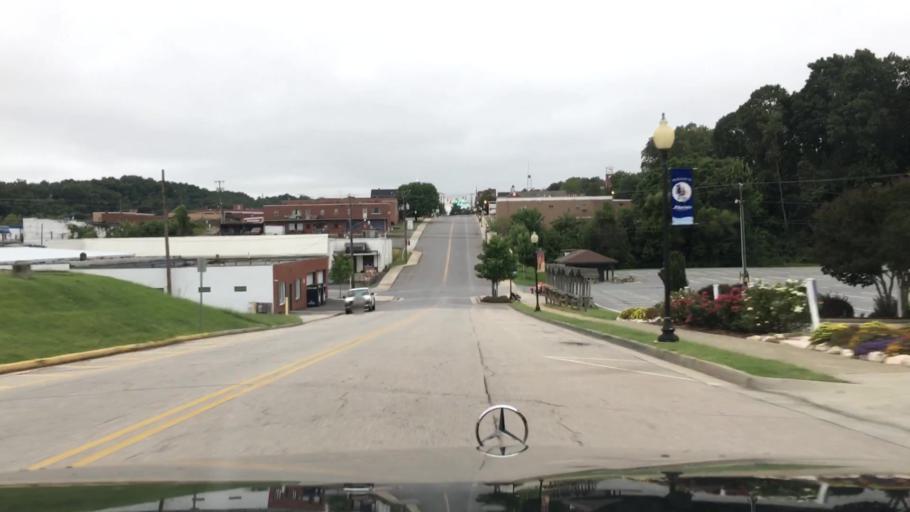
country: US
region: Virginia
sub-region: Campbell County
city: Altavista
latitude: 37.1120
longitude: -79.2870
